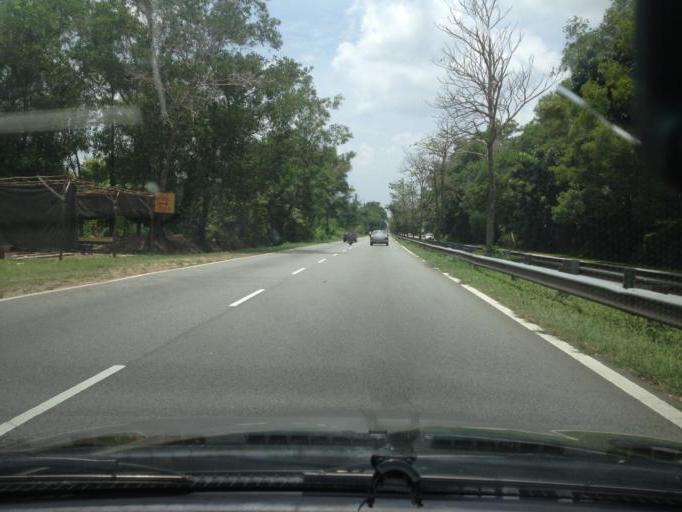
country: MY
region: Kedah
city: Sungai Petani
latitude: 5.6442
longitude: 100.5393
